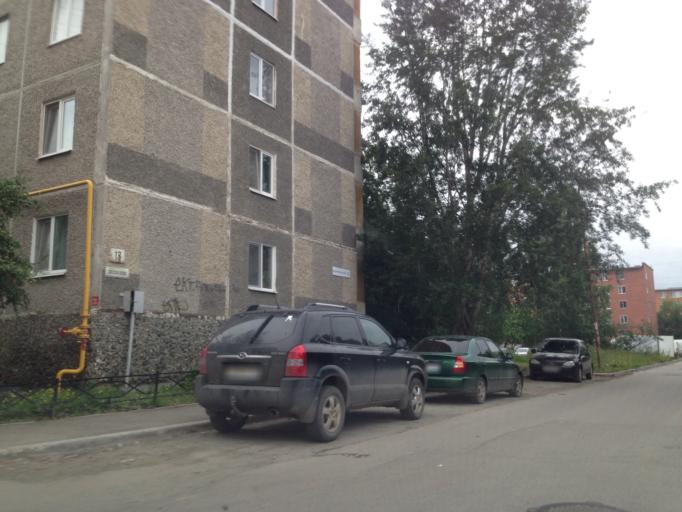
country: RU
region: Sverdlovsk
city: Yekaterinburg
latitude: 56.8305
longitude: 60.6880
